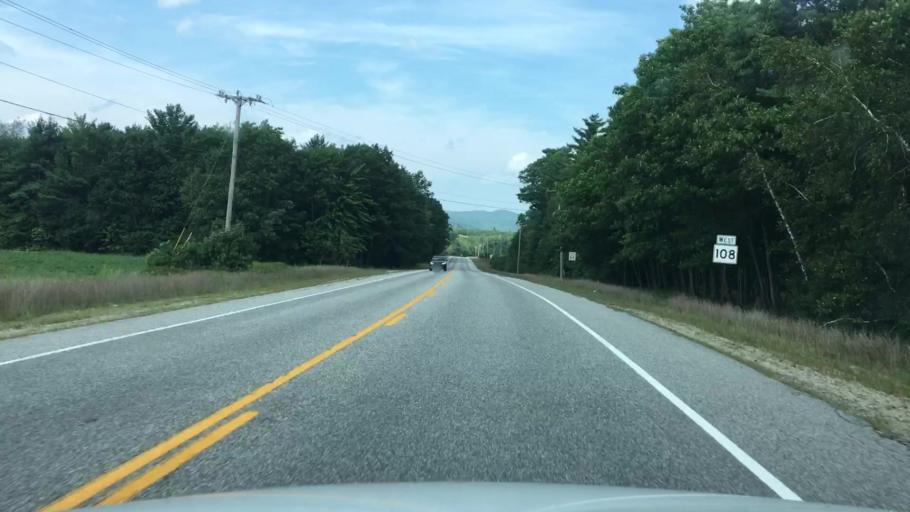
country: US
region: Maine
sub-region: Oxford County
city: Canton
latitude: 44.4665
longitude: -70.3220
